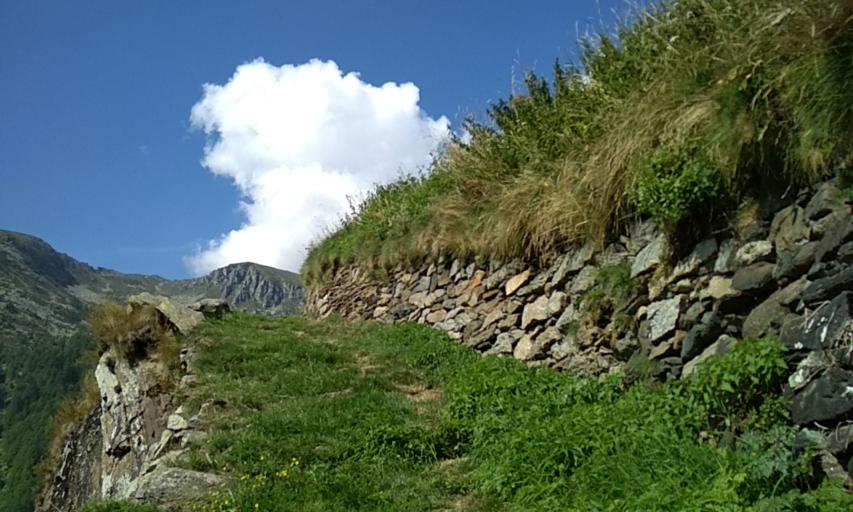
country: IT
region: Piedmont
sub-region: Provincia di Torino
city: Noasca
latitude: 45.4581
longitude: 7.2880
